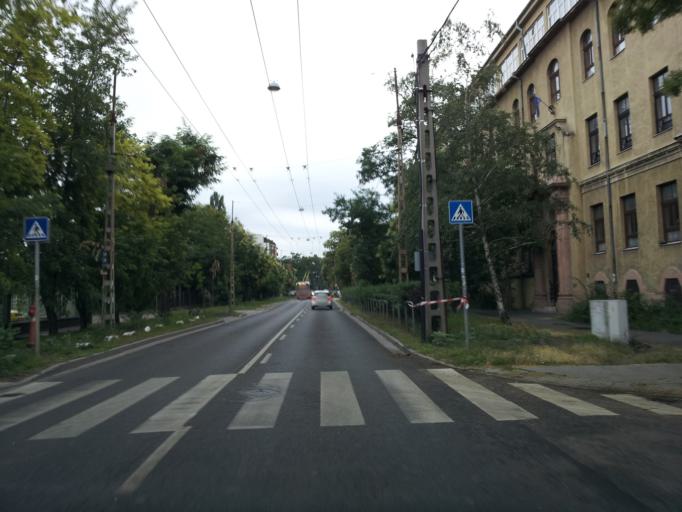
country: HU
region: Budapest
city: Budapest XIV. keruelet
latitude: 47.5126
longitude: 19.1167
